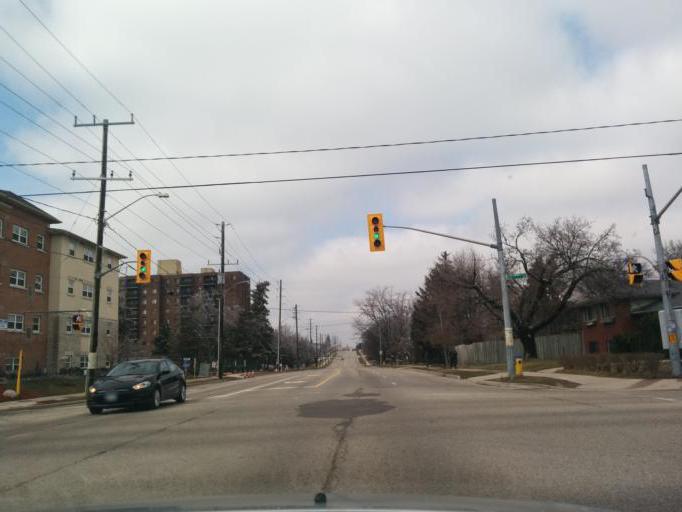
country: CA
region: Ontario
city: Waterloo
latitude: 43.4786
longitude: -80.5352
